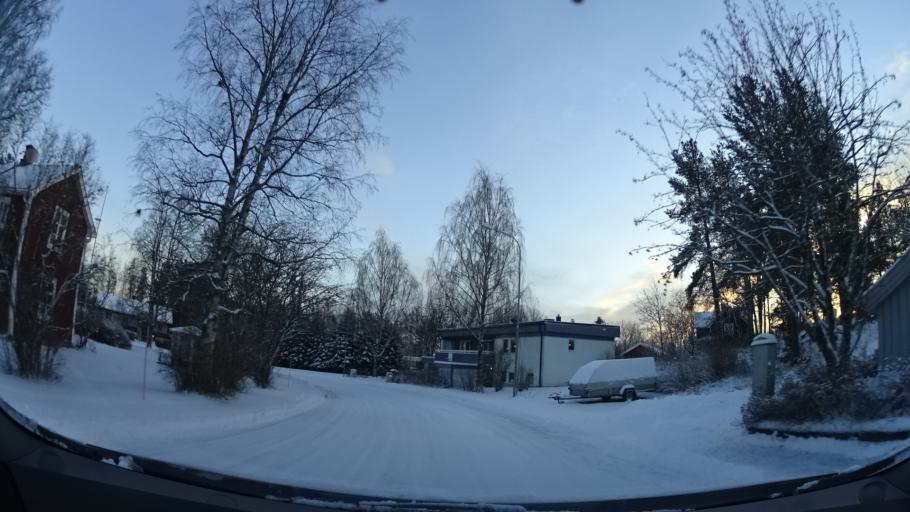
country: SE
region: Vaesterbotten
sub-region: Skelleftea Kommun
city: Kage
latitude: 64.8413
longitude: 20.9837
